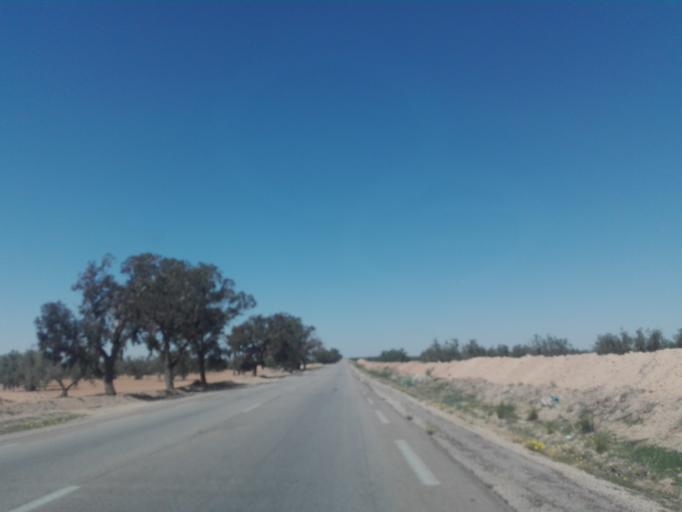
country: TN
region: Safaqis
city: Bi'r `Ali Bin Khalifah
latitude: 34.7571
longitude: 10.3225
